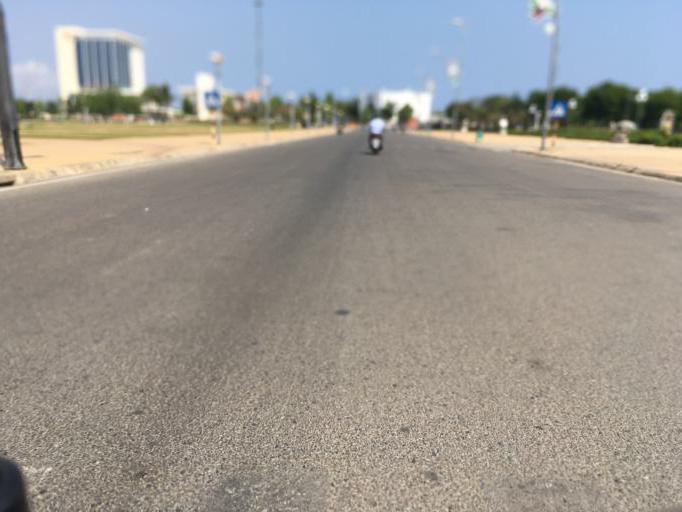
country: VN
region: Ninh Thuan
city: Phan Rang-Thap Cham
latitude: 11.5651
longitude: 108.9987
